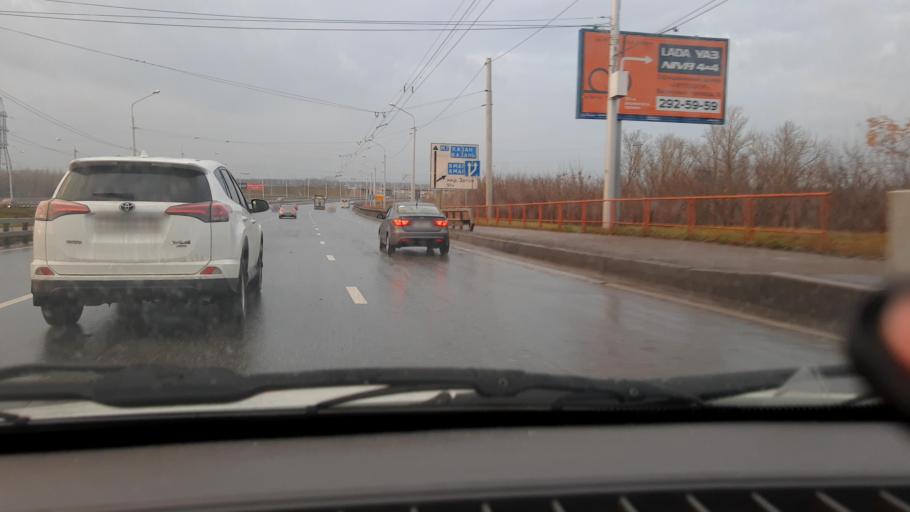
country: RU
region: Bashkortostan
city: Ufa
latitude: 54.7605
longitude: 55.9612
